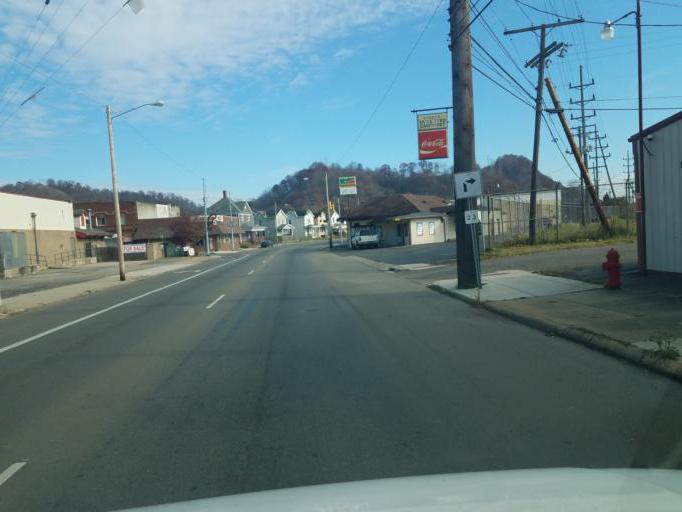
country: US
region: Ohio
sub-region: Scioto County
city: New Boston
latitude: 38.7537
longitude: -82.9331
